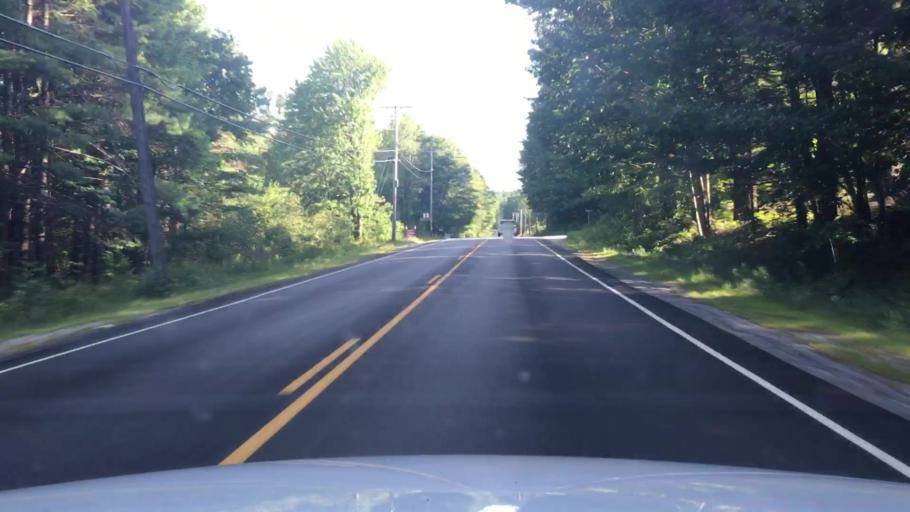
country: US
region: Maine
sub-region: Cumberland County
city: Cumberland Center
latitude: 43.8382
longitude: -70.3213
